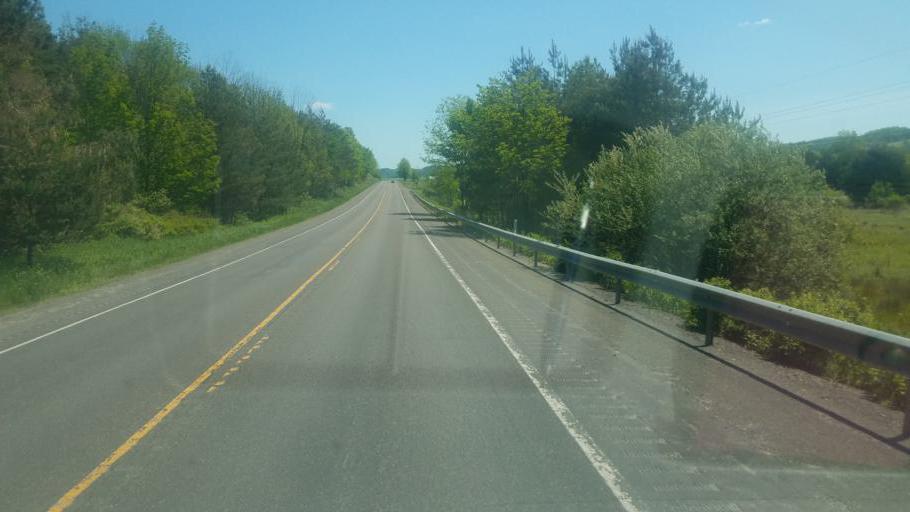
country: US
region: Pennsylvania
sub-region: Tioga County
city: Wellsboro
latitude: 41.7662
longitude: -77.1970
